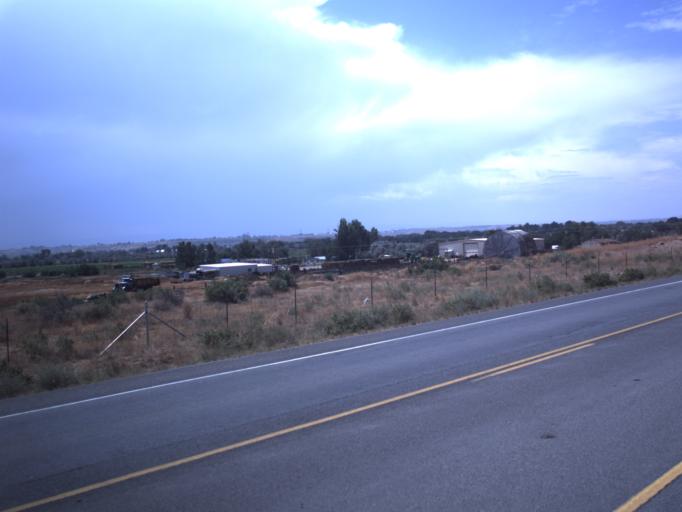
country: US
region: Utah
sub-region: Duchesne County
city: Roosevelt
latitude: 40.3023
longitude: -109.9502
